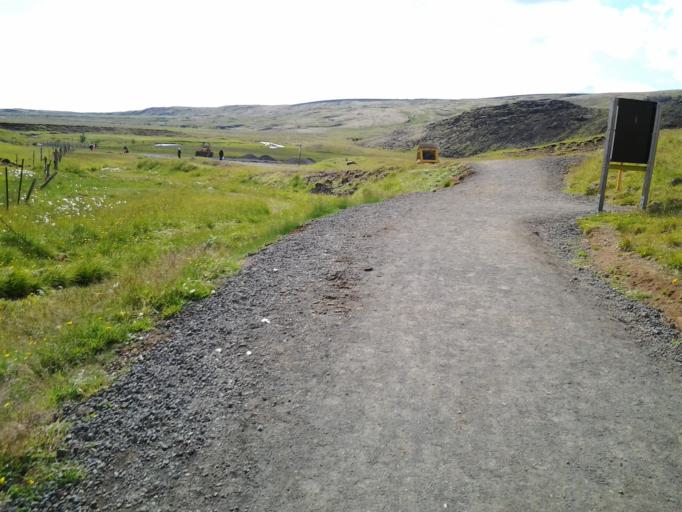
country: IS
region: South
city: Hveragerdi
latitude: 64.0248
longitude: -21.2129
